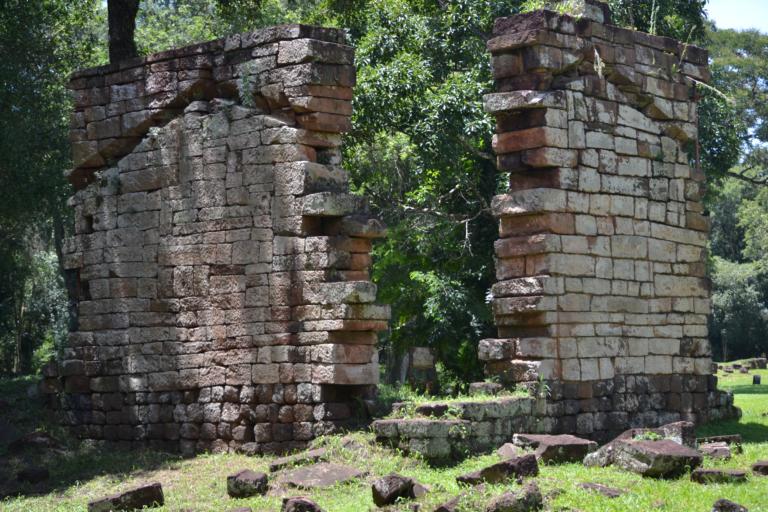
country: AR
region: Misiones
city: Santa Ana
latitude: -27.3896
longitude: -55.5808
